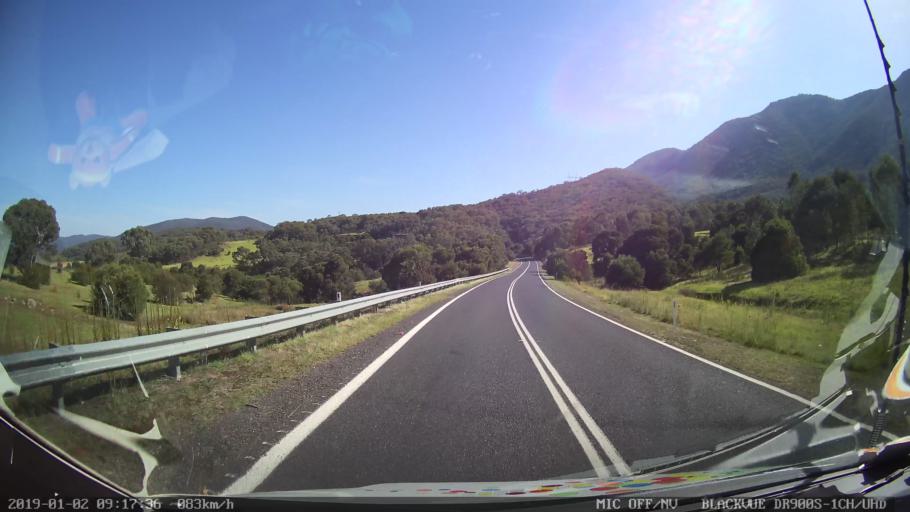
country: AU
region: New South Wales
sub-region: Tumut Shire
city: Tumut
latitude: -35.4380
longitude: 148.2863
